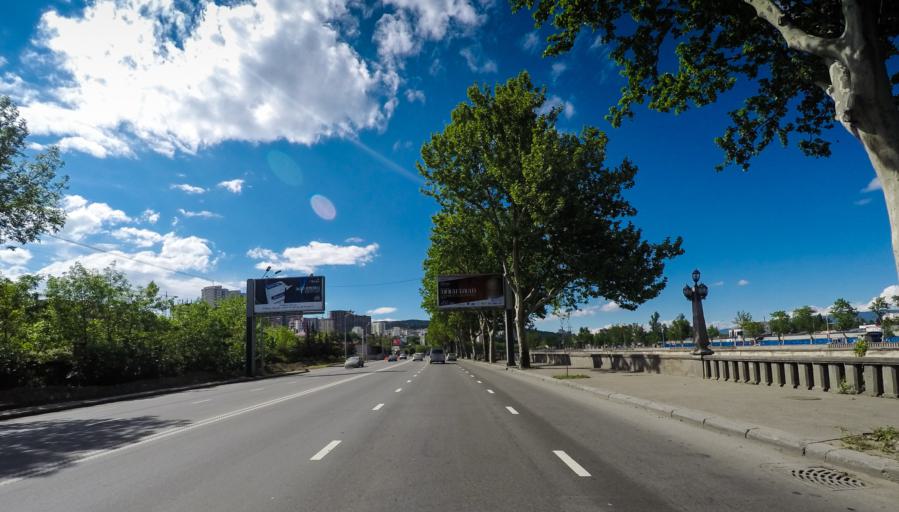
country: GE
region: T'bilisi
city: Tbilisi
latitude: 41.7277
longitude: 44.7791
